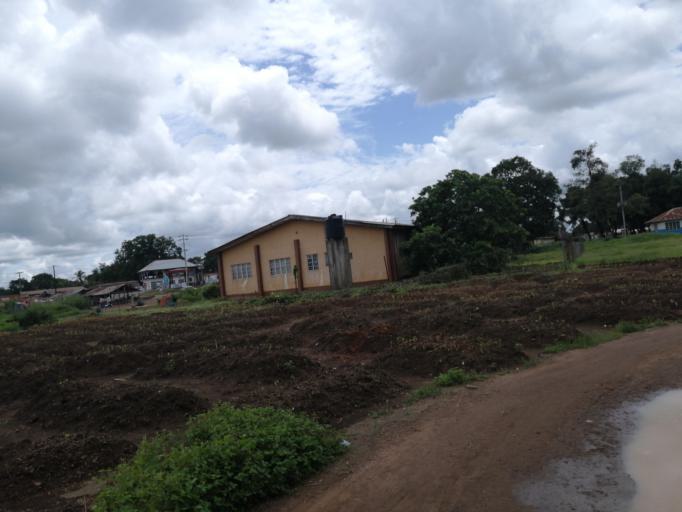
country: SL
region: Northern Province
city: Port Loko
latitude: 8.7736
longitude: -12.7866
